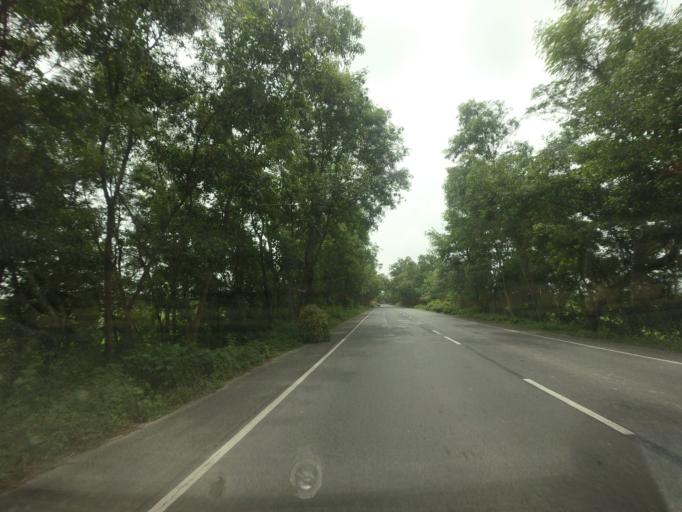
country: BD
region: Khulna
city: Kalia
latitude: 23.2342
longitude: 89.7434
